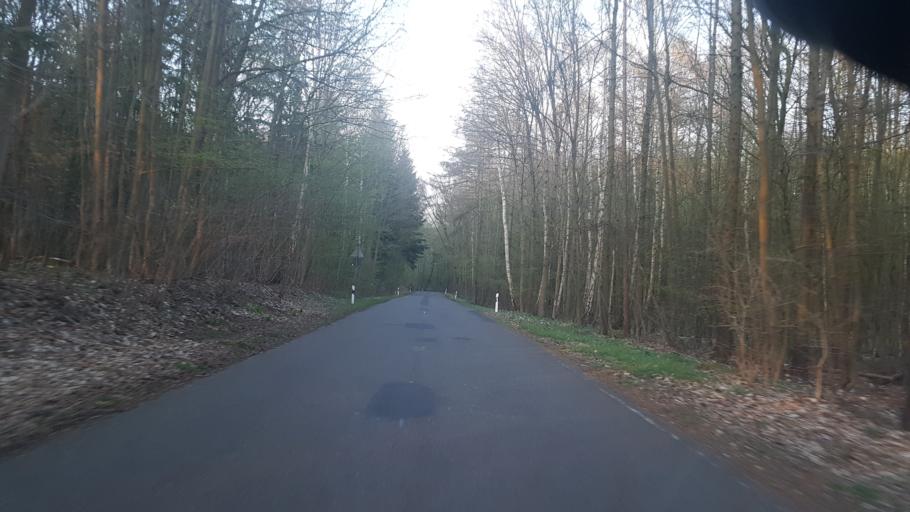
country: DE
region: Brandenburg
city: Gramzow
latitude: 53.1756
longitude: 13.8994
